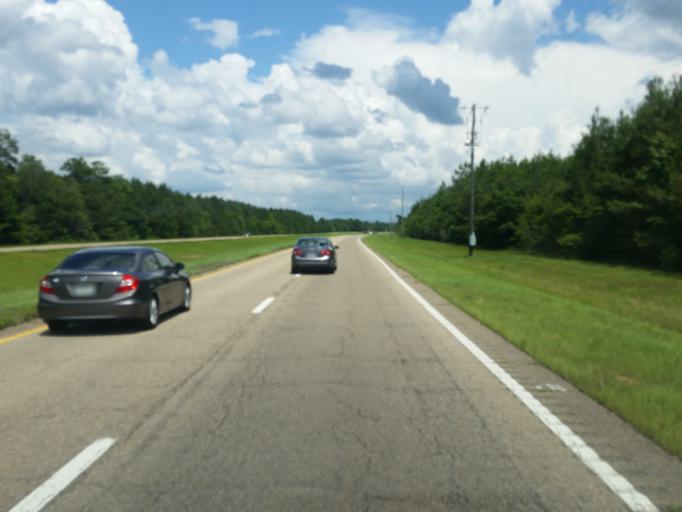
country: US
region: Mississippi
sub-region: Perry County
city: New Augusta
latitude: 31.1442
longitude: -88.8762
